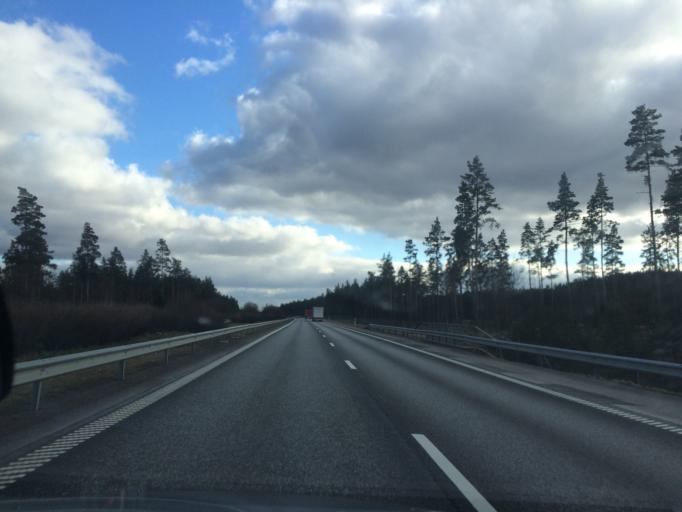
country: SE
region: Joenkoeping
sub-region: Vaggeryds Kommun
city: Skillingaryd
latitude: 57.3796
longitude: 14.1000
